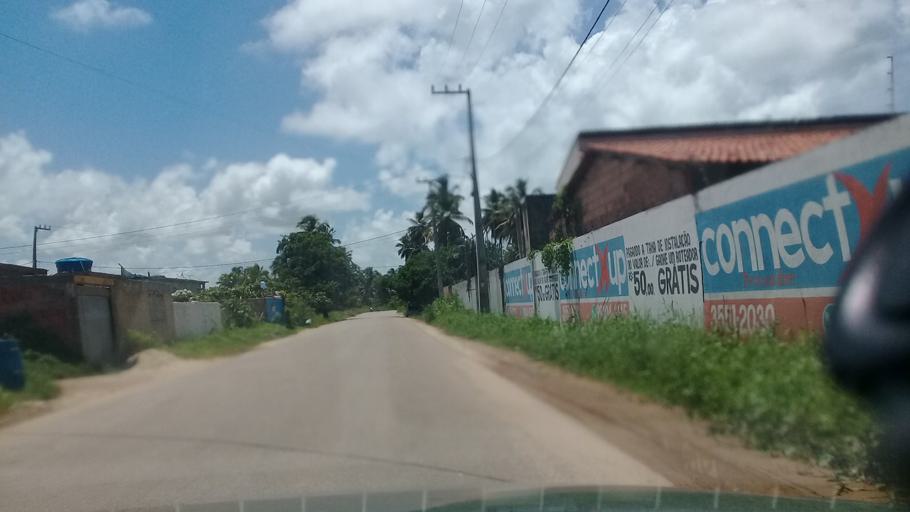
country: BR
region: Pernambuco
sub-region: Sirinhaem
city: Sirinhaem
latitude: -8.6205
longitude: -35.0595
